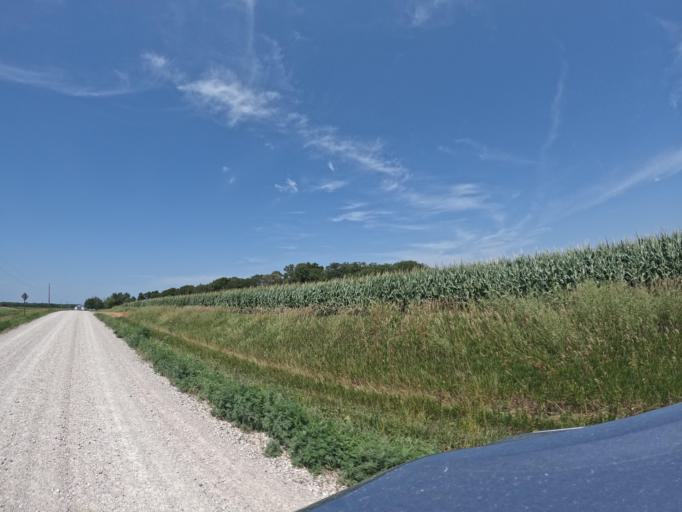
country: US
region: Iowa
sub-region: Henry County
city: Mount Pleasant
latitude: 40.9126
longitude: -91.6564
